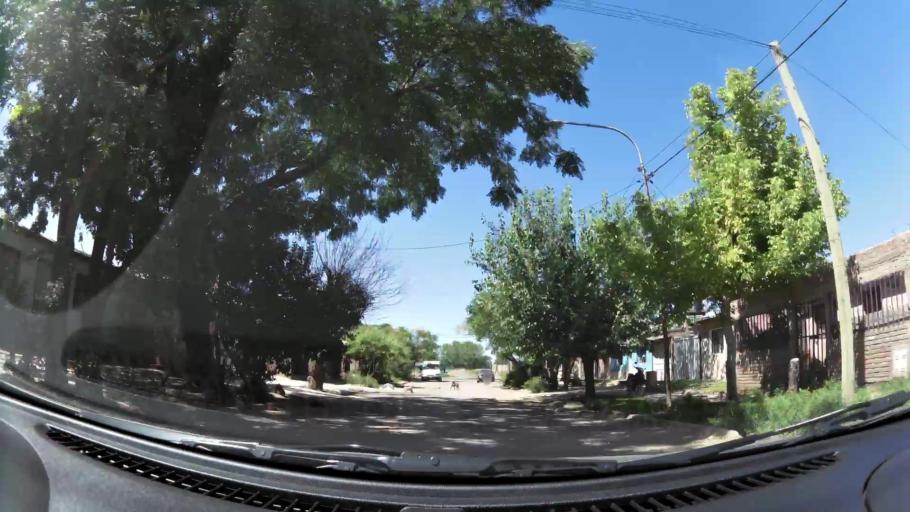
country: AR
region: Mendoza
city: Villa Nueva
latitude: -32.8761
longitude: -68.7872
